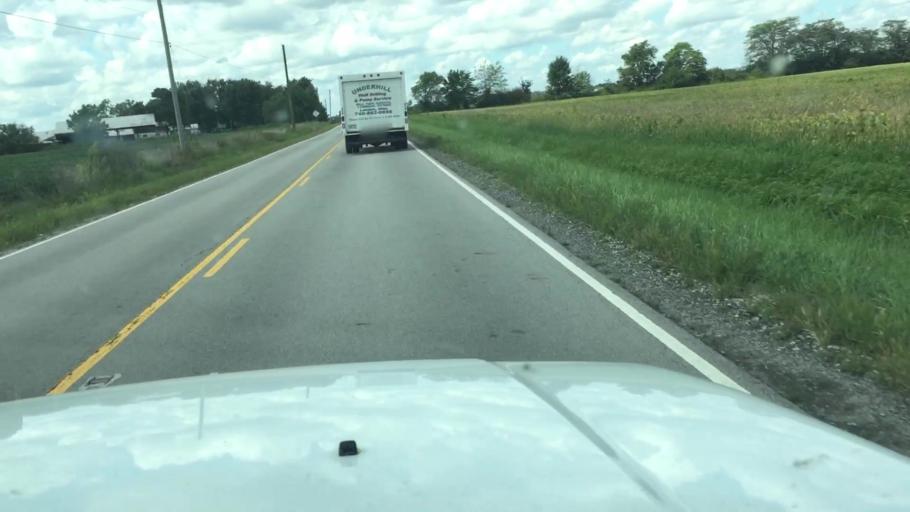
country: US
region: Ohio
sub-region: Madison County
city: Bethel
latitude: 39.8259
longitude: -83.3625
